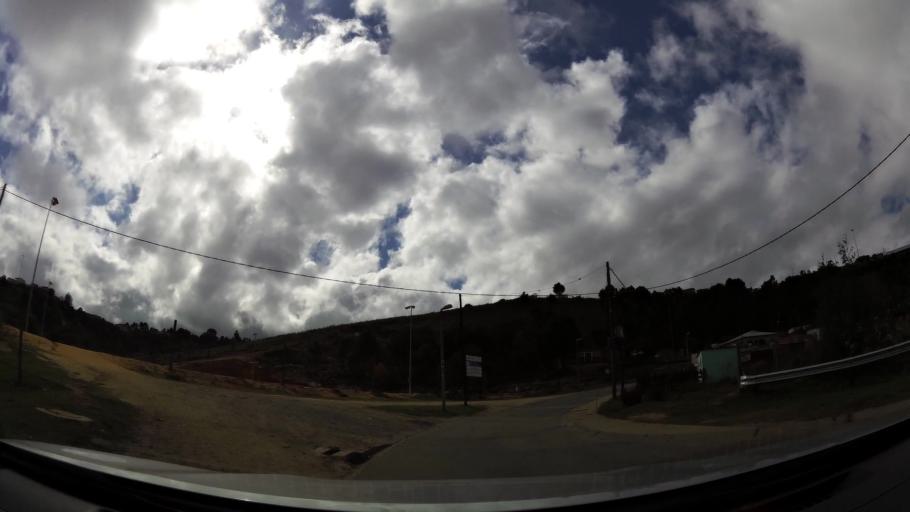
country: ZA
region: Western Cape
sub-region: Eden District Municipality
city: Knysna
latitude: -34.0334
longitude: 23.1029
